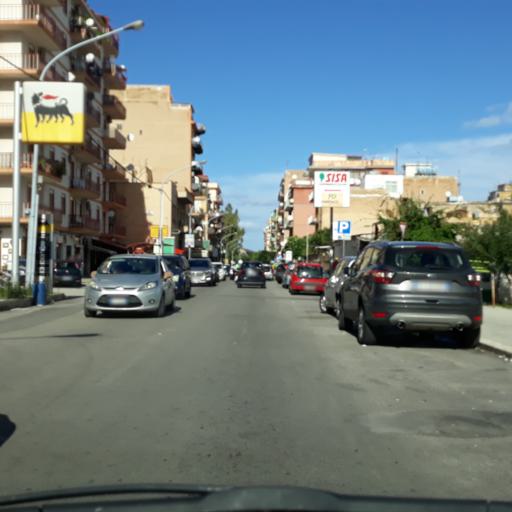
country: IT
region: Sicily
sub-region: Palermo
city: Palermo
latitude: 38.1509
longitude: 13.3707
